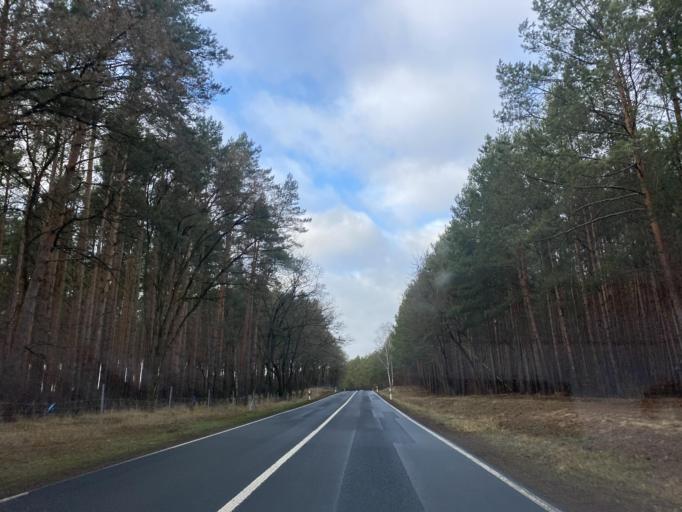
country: PL
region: Lubusz
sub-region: Powiat zarski
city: Leknica
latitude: 51.4967
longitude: 14.8229
